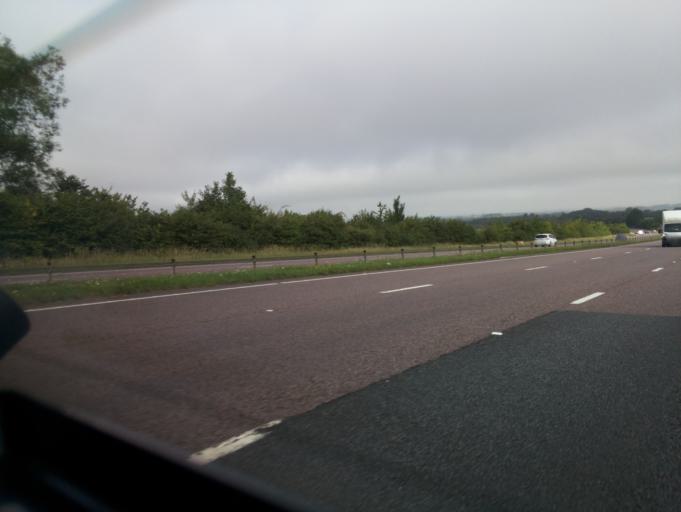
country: GB
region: England
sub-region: Borough of Swindon
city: Broad Blunsdon
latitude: 51.6159
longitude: -1.8020
